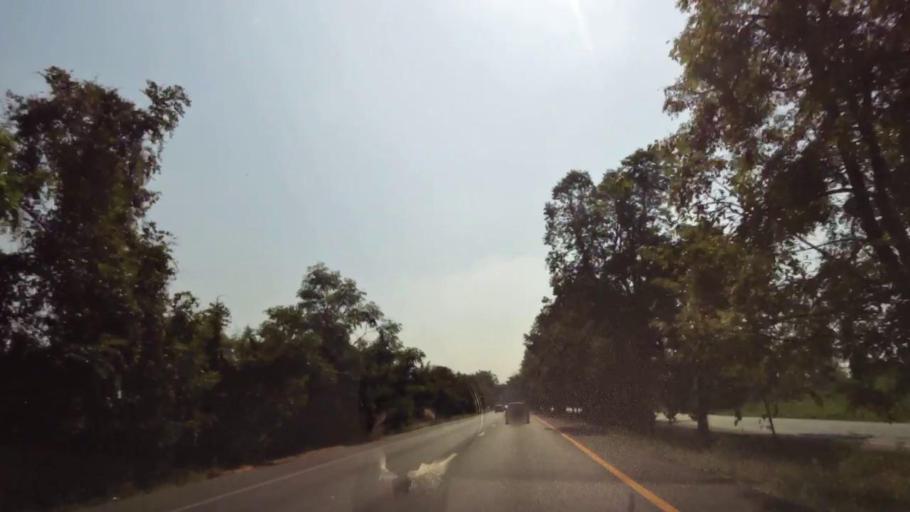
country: TH
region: Phichit
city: Bueng Na Rang
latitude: 16.0291
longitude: 100.1152
